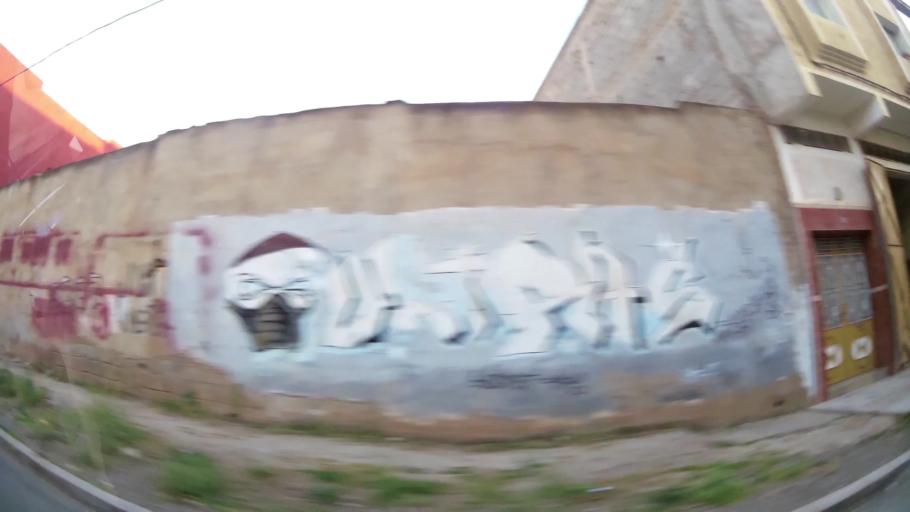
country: MA
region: Oriental
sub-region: Berkane-Taourirt
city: Berkane
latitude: 34.9186
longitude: -2.3130
